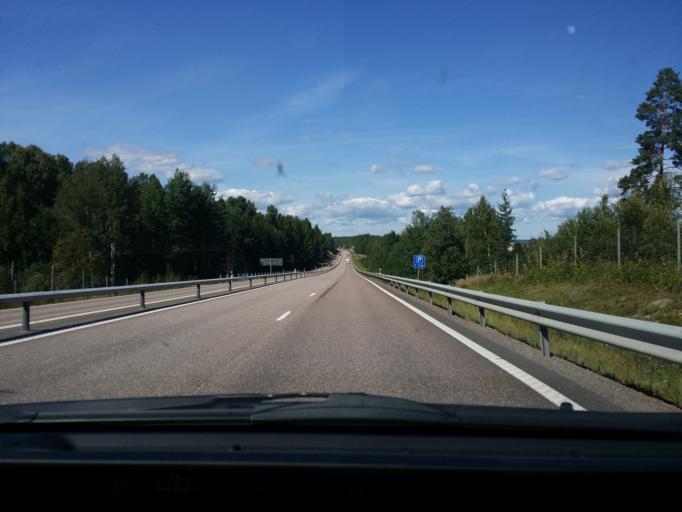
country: SE
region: Dalarna
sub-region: Hedemora Kommun
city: Brunna
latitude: 60.2329
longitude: 16.0338
